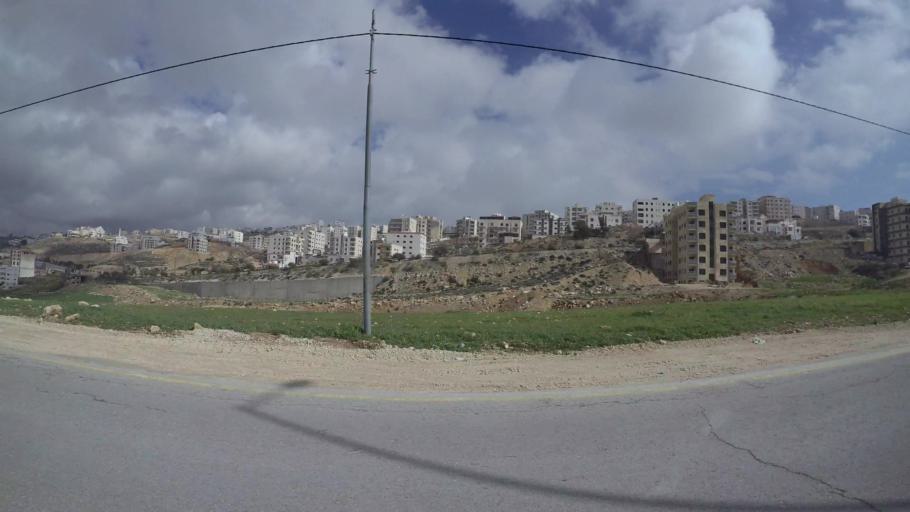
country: JO
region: Amman
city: Al Jubayhah
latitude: 32.0663
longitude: 35.8690
